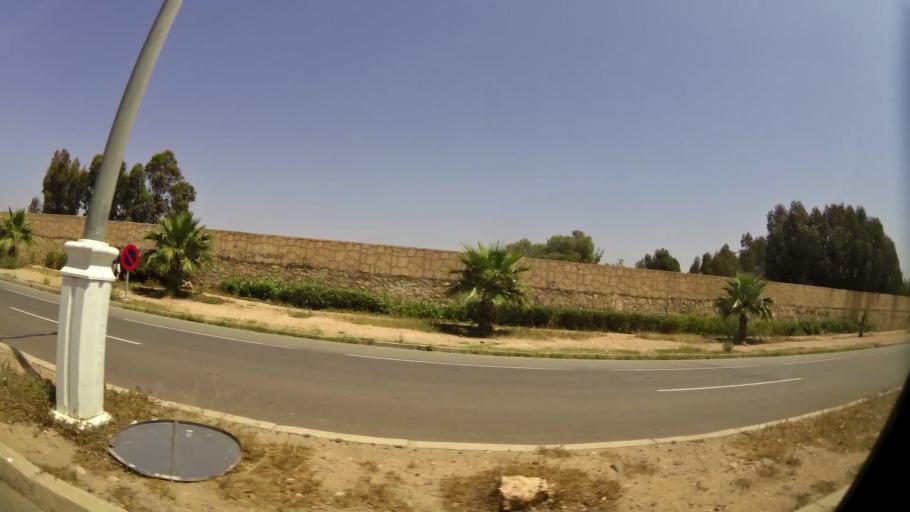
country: MA
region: Souss-Massa-Draa
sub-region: Inezgane-Ait Mellou
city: Inezgane
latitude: 30.3521
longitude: -9.4873
